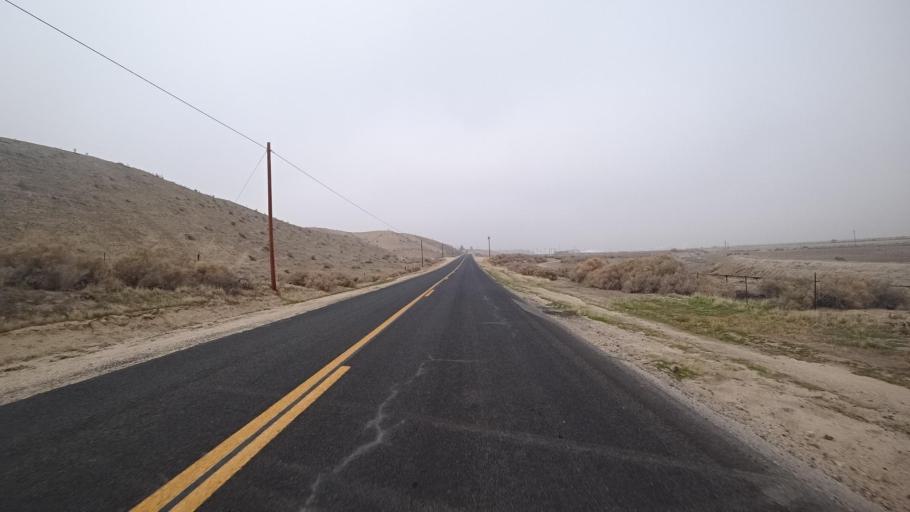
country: US
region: California
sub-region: Kern County
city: Ford City
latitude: 35.2581
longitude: -119.3096
